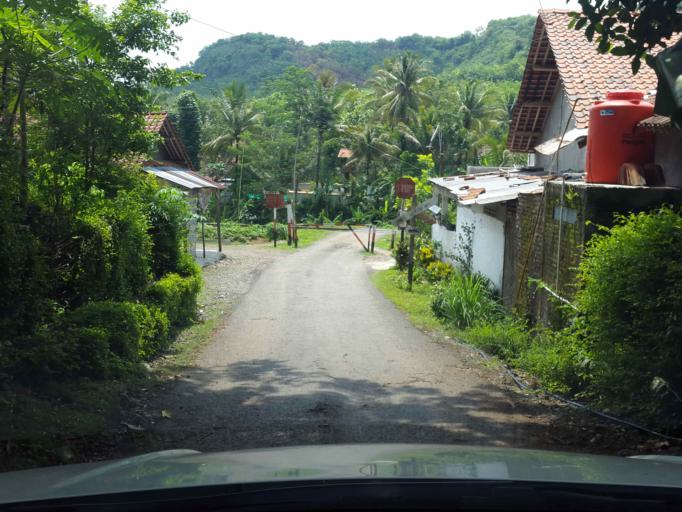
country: ID
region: Central Java
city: Cilongkrang
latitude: -7.4120
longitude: 108.7238
